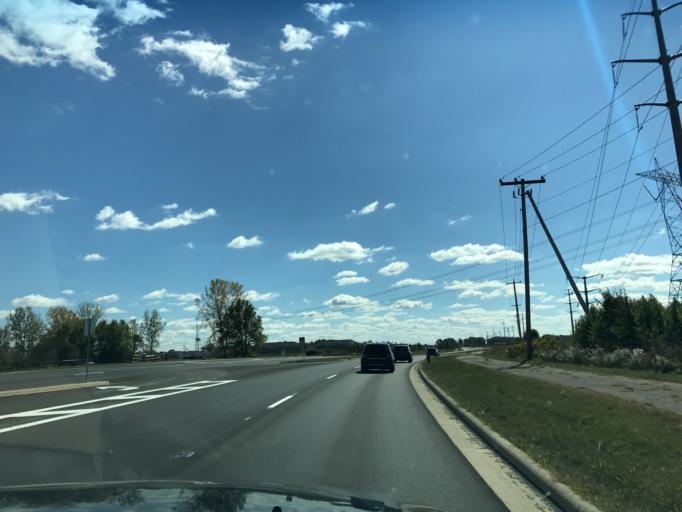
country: US
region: Ohio
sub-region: Delaware County
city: Powell
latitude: 40.2082
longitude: -83.0957
